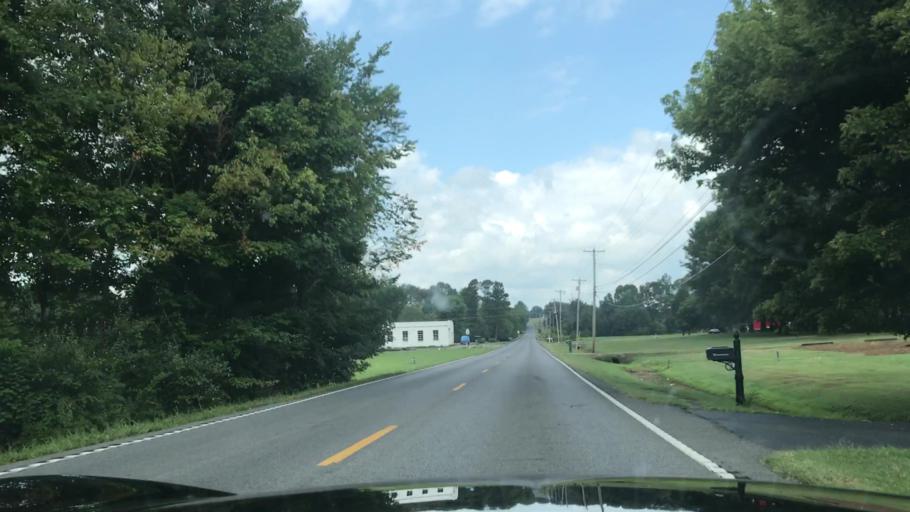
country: US
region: Kentucky
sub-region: Muhlenberg County
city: Greenville
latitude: 37.2001
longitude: -87.1347
